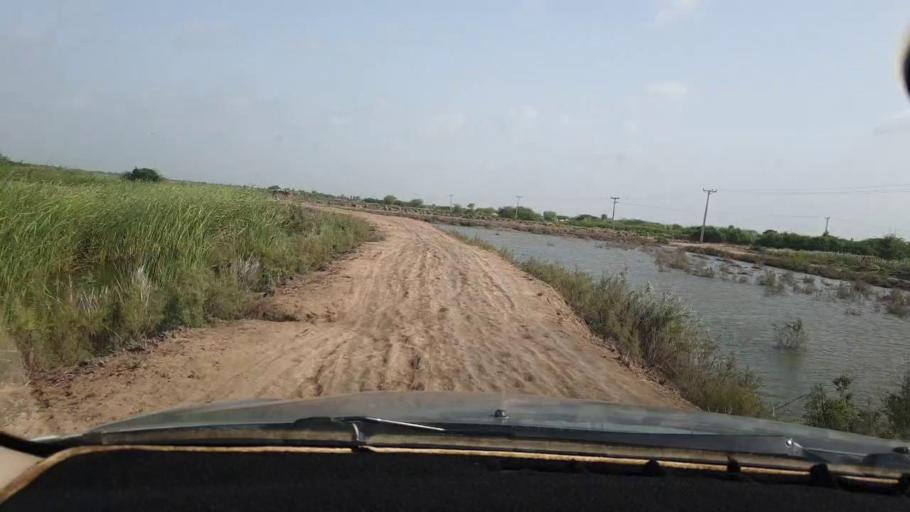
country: PK
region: Sindh
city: Tando Bago
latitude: 24.8153
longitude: 68.9363
